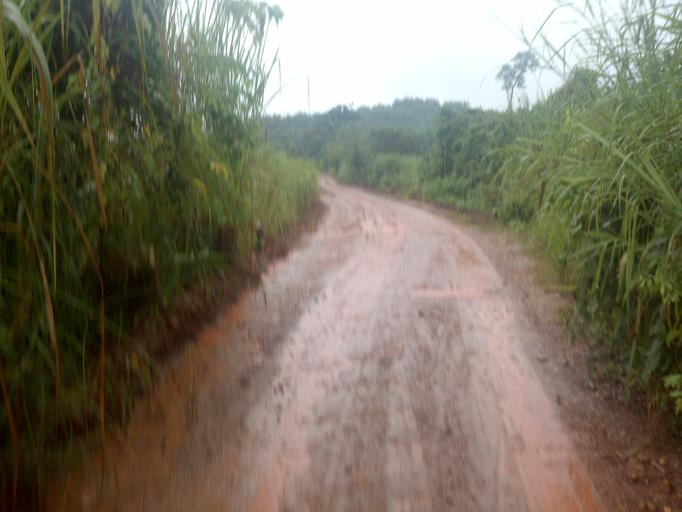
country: LA
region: Bolikhamxai
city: Bolikhan
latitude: 18.5351
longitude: 103.8172
